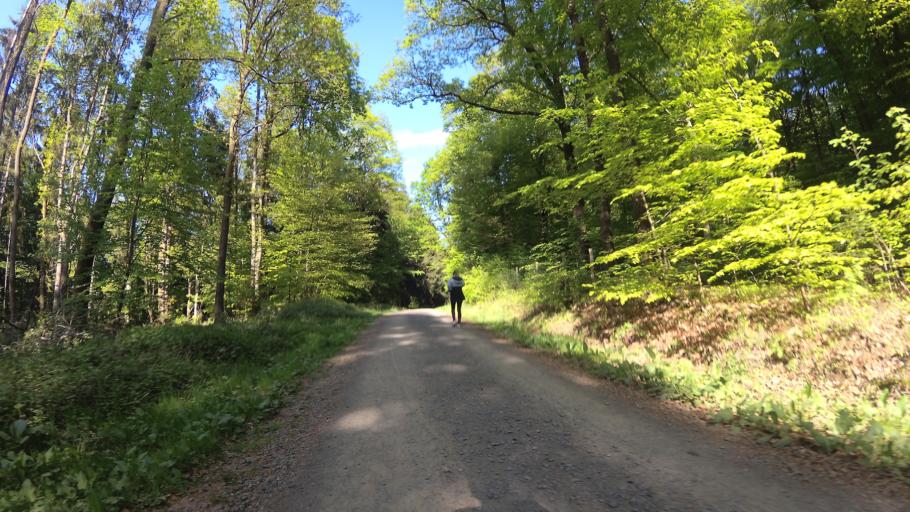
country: DE
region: Saarland
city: Mainzweiler
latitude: 49.3980
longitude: 7.1349
